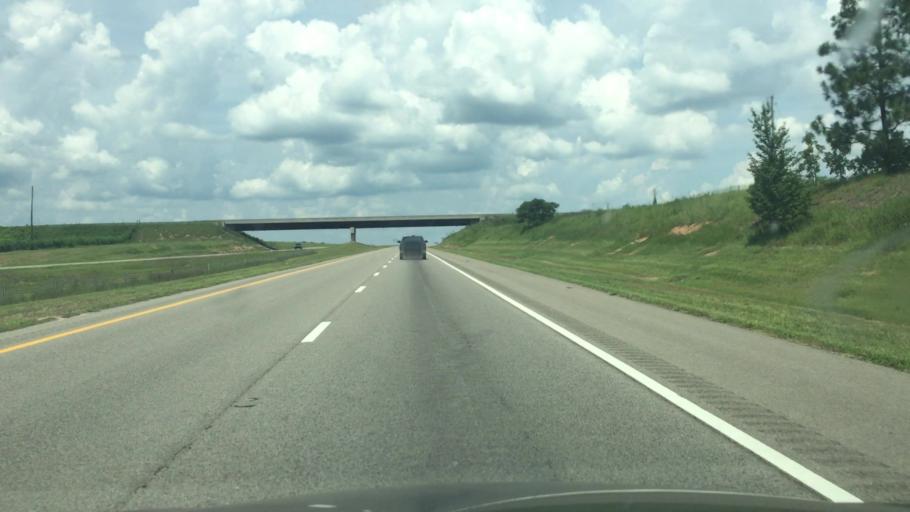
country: US
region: North Carolina
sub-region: Richmond County
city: Ellerbe
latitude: 35.1855
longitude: -79.7199
